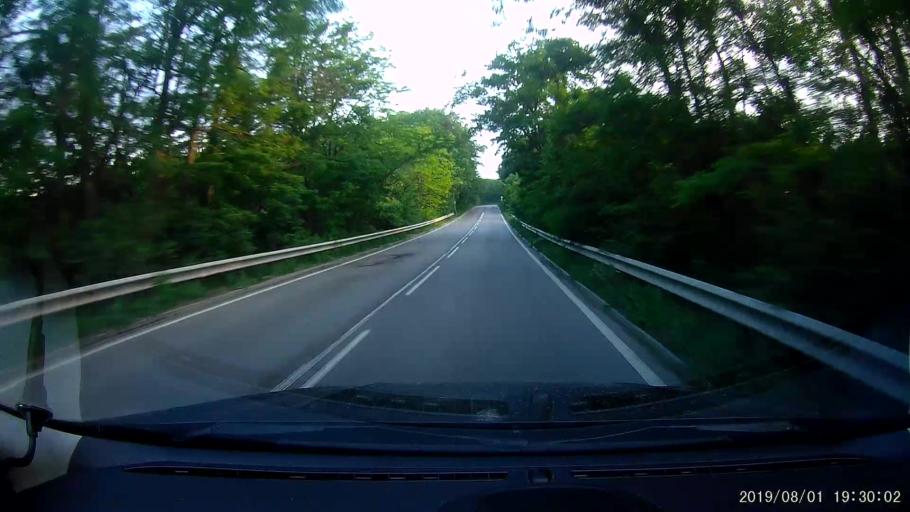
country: BG
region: Burgas
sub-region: Obshtina Sungurlare
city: Sungurlare
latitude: 42.8191
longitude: 26.8967
